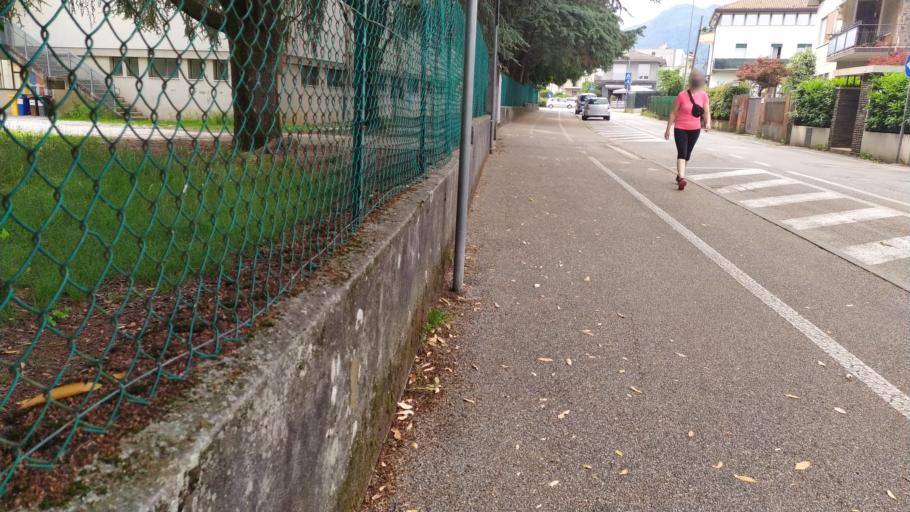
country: IT
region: Veneto
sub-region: Provincia di Vicenza
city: Schio
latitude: 45.7037
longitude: 11.3525
